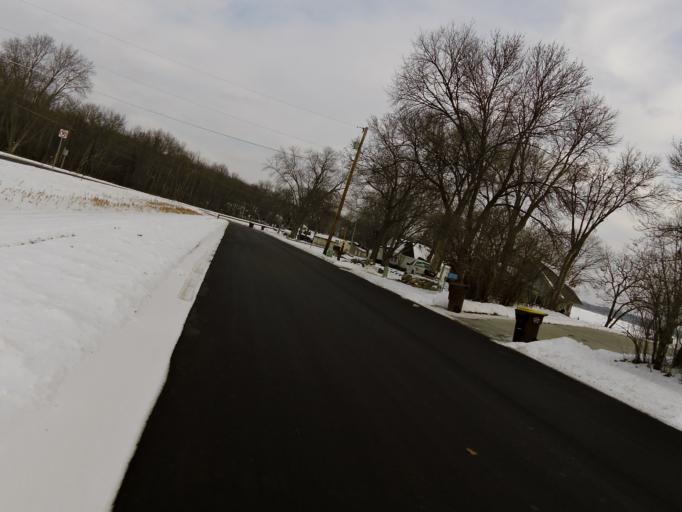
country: US
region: Minnesota
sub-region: Scott County
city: Prior Lake
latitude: 44.7049
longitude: -93.4852
